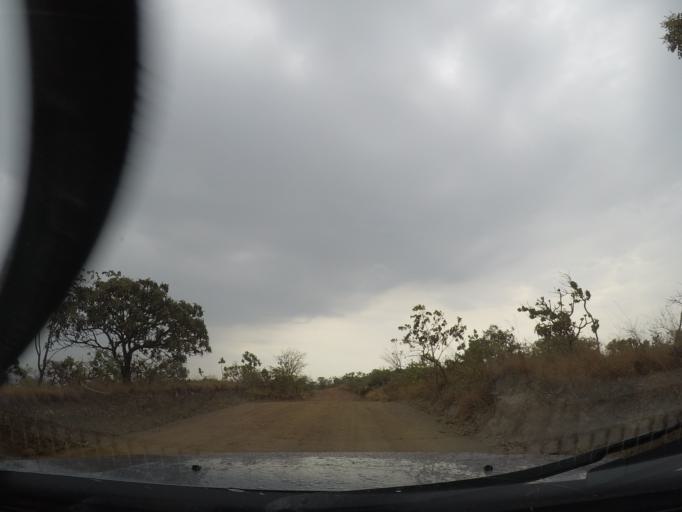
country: BR
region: Goias
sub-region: Pirenopolis
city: Pirenopolis
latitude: -15.8282
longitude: -48.9045
